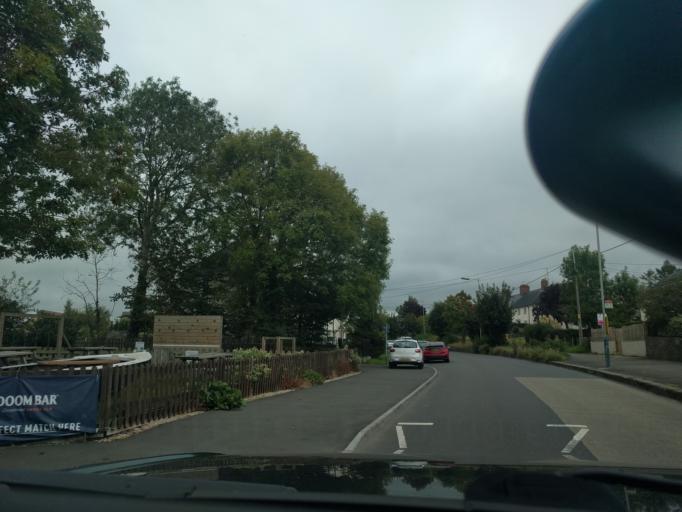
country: GB
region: England
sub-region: Wiltshire
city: Chippenham
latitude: 51.4520
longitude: -2.1055
